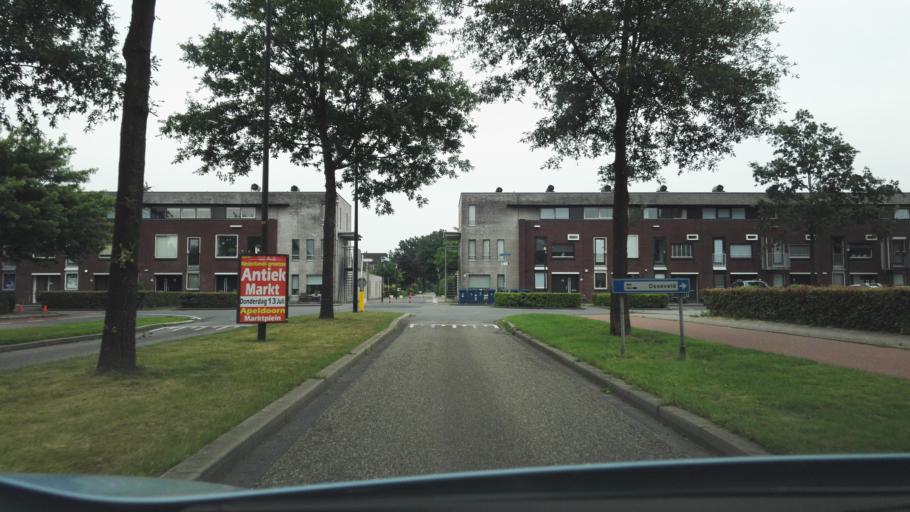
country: NL
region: Gelderland
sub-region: Gemeente Apeldoorn
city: Apeldoorn
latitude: 52.2181
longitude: 6.0041
